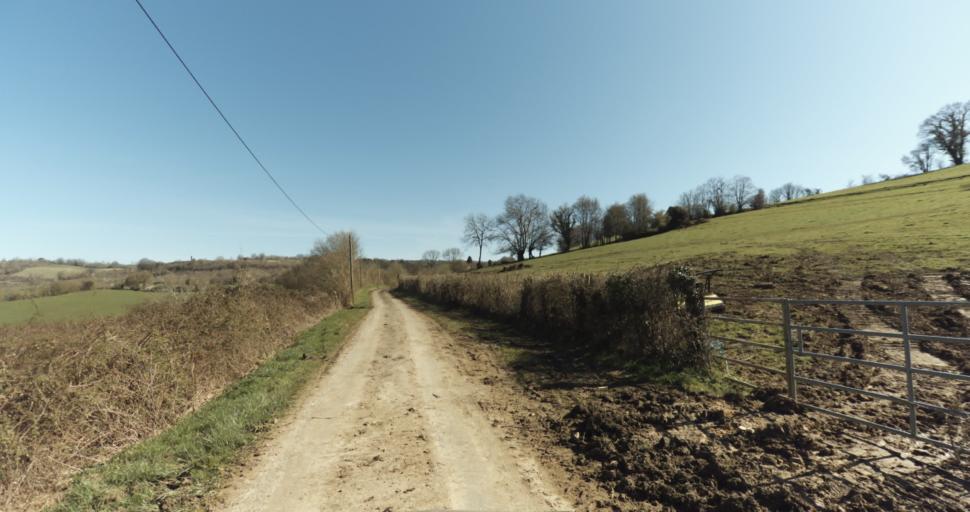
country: FR
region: Lower Normandy
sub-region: Departement du Calvados
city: Livarot
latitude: 48.9509
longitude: 0.0683
